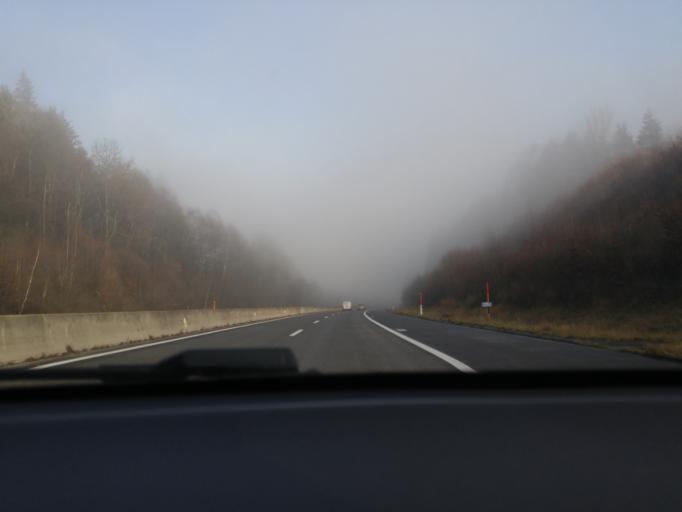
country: AT
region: Upper Austria
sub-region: Politischer Bezirk Vocklabruck
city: Attersee
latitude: 47.9523
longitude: 13.5283
